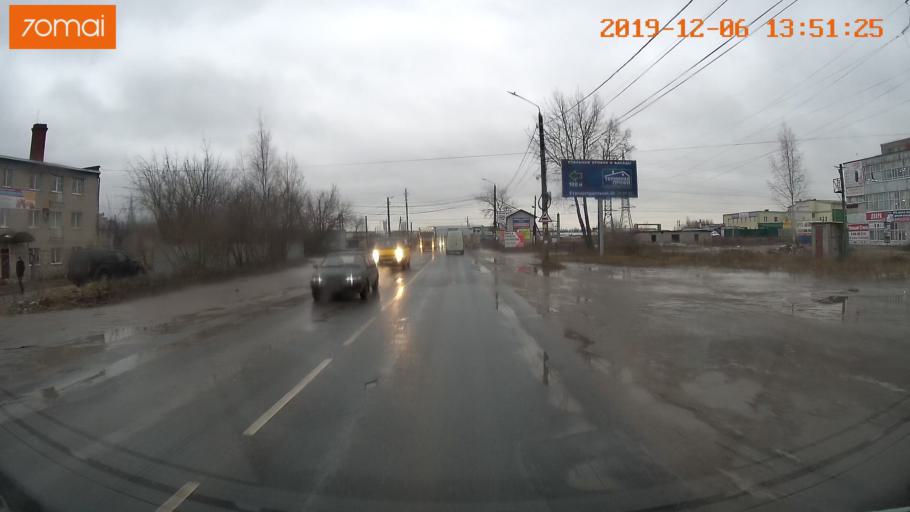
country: RU
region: Ivanovo
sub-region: Gorod Ivanovo
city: Ivanovo
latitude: 56.9682
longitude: 40.9524
